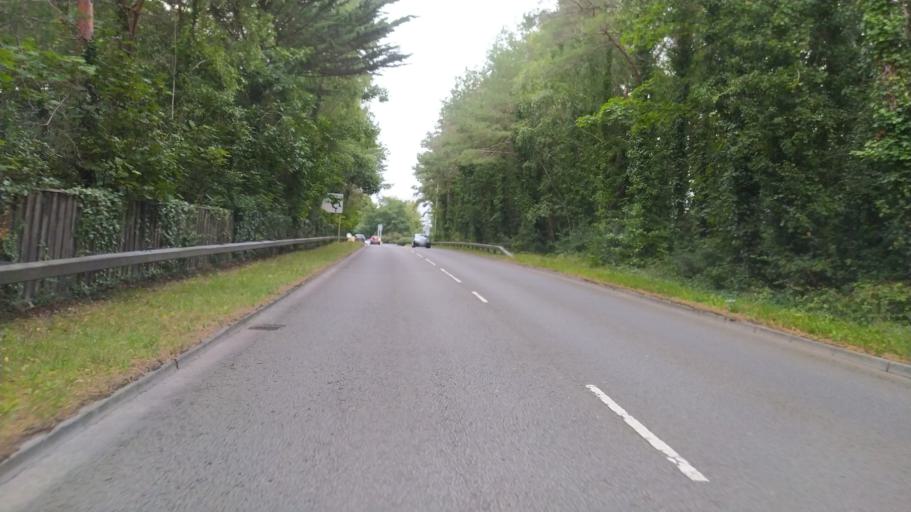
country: GB
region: England
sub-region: Dorset
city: Broadstone
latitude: 50.7605
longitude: -1.9970
